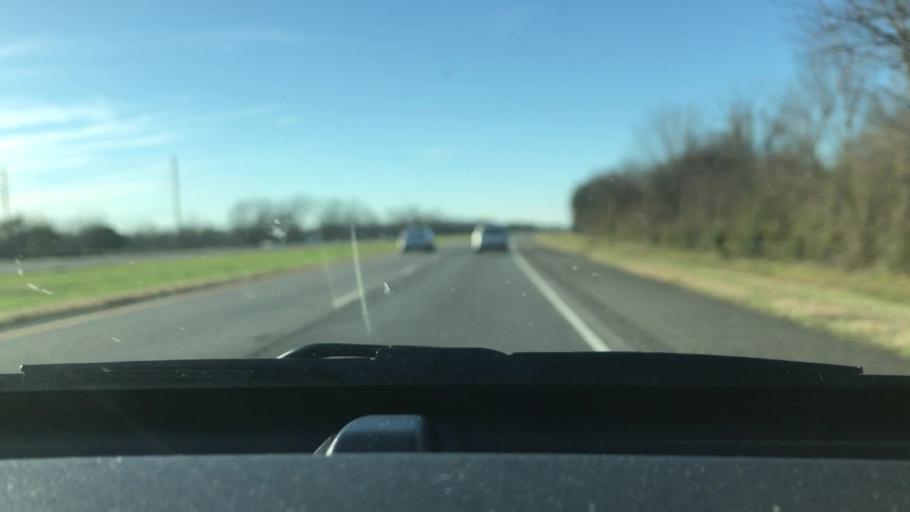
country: US
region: Louisiana
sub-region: Rapides Parish
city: Boyce
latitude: 31.3722
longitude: -92.6284
